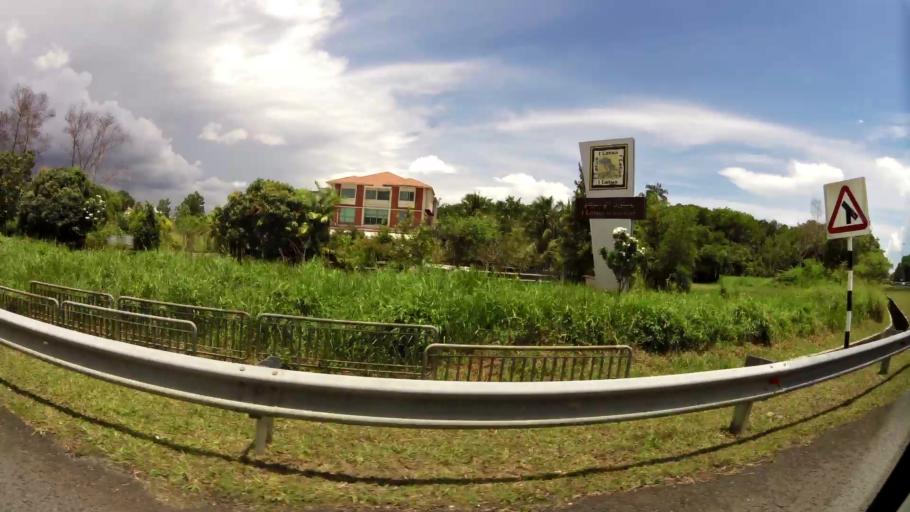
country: BN
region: Brunei and Muara
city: Bandar Seri Begawan
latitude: 4.9447
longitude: 114.9074
